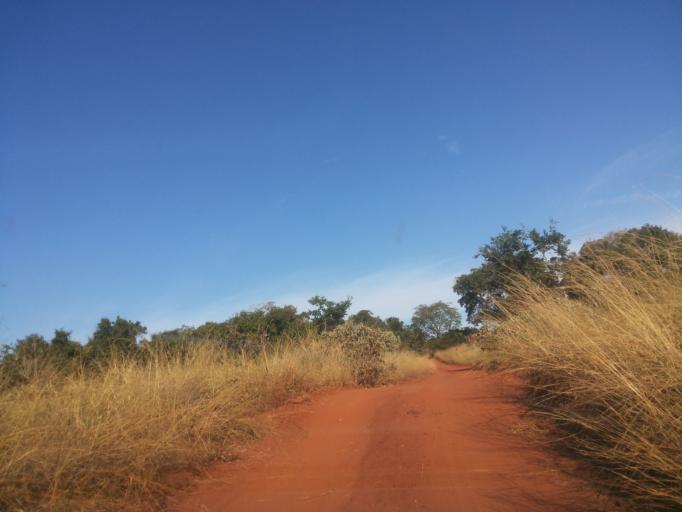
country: BR
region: Minas Gerais
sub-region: Ituiutaba
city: Ituiutaba
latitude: -19.0972
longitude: -49.4155
